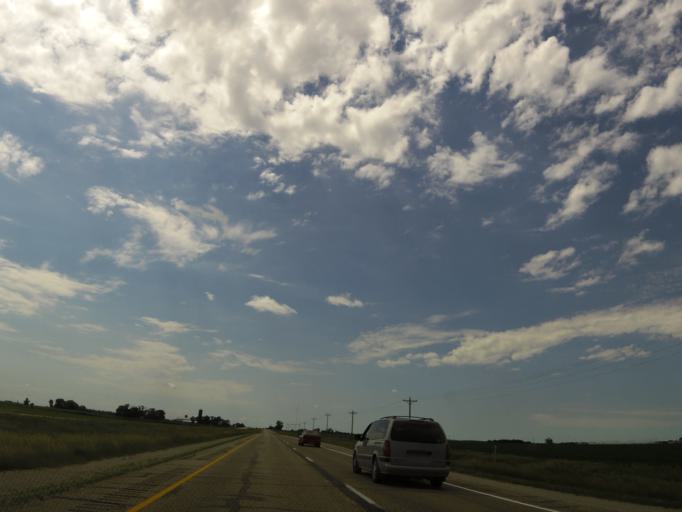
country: US
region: Iowa
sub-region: Bremer County
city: Tripoli
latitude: 42.7940
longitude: -92.3374
